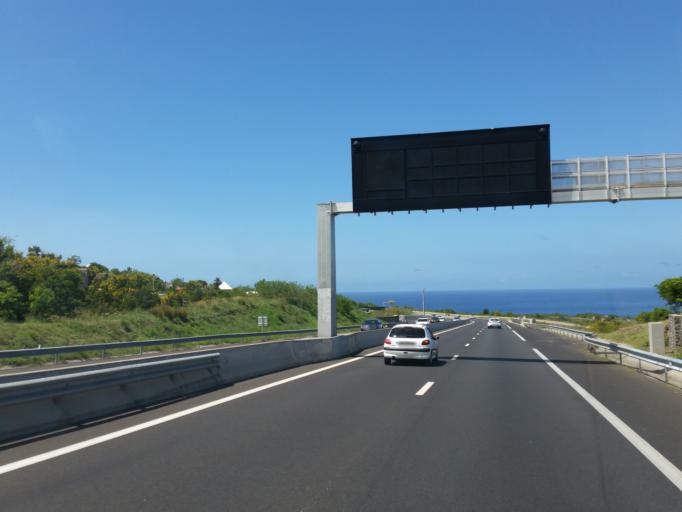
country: RE
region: Reunion
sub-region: Reunion
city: Saint-Leu
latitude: -21.1985
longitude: 55.2948
